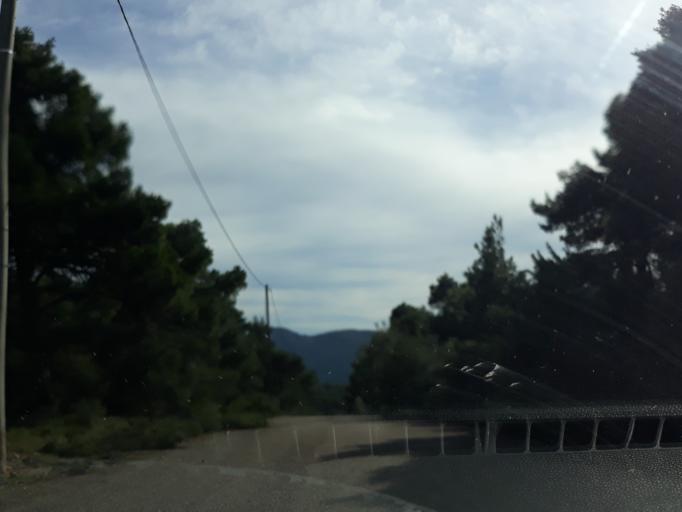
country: GR
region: Attica
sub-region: Nomarchia Anatolikis Attikis
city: Afidnes
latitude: 38.2174
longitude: 23.7954
